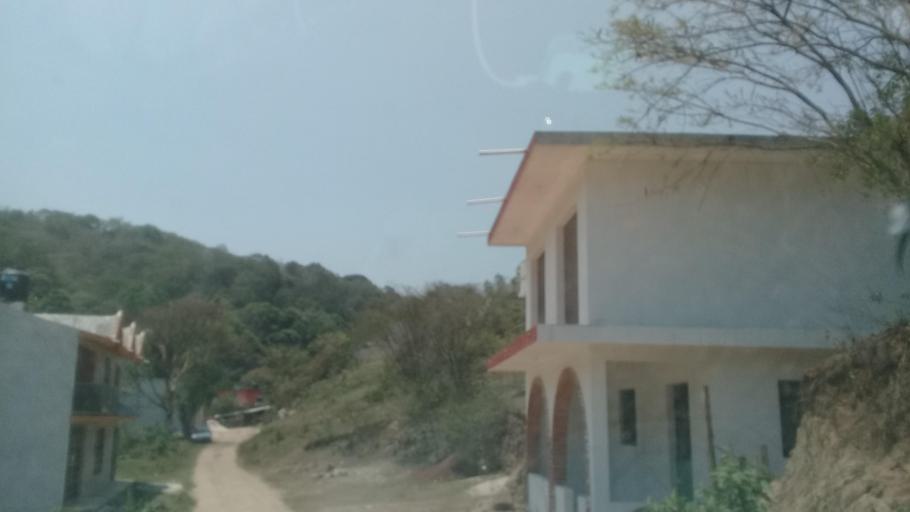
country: MX
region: Veracruz
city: El Castillo
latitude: 19.5565
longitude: -96.8564
